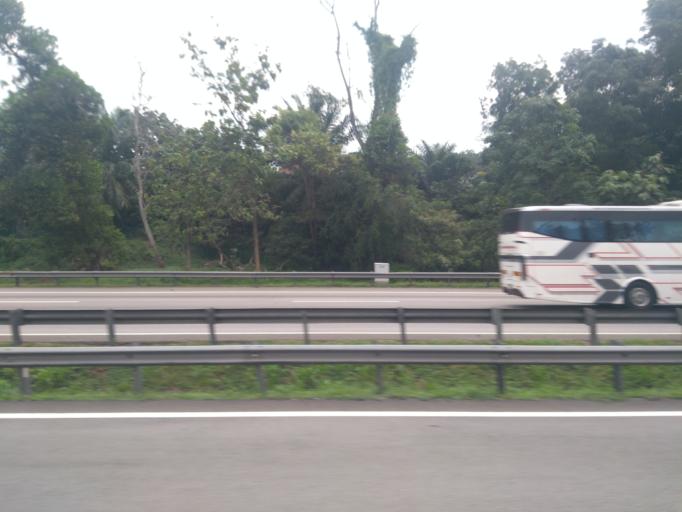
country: MY
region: Negeri Sembilan
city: Seremban
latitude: 2.6522
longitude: 101.9910
